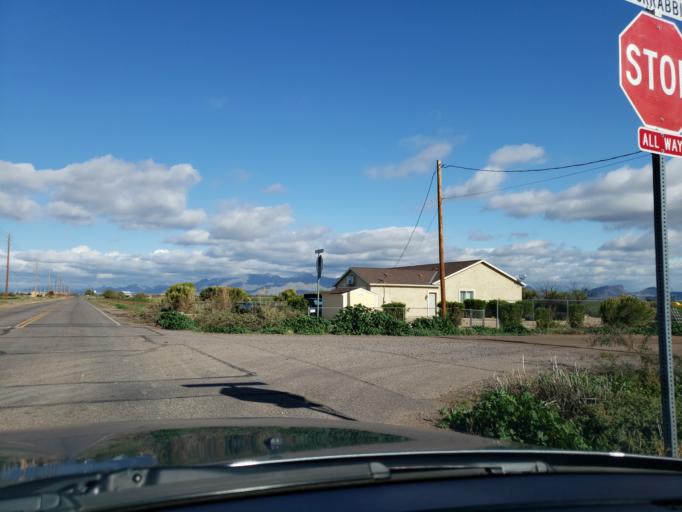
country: US
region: Arizona
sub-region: Maricopa County
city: Scottsdale
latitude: 33.5166
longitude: -111.8740
